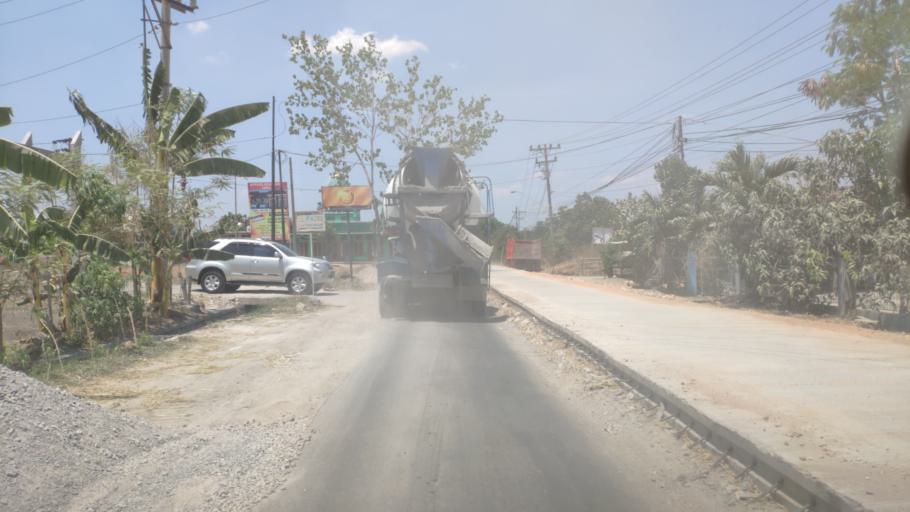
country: ID
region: Central Java
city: Cepu
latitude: -7.1411
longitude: 111.5782
